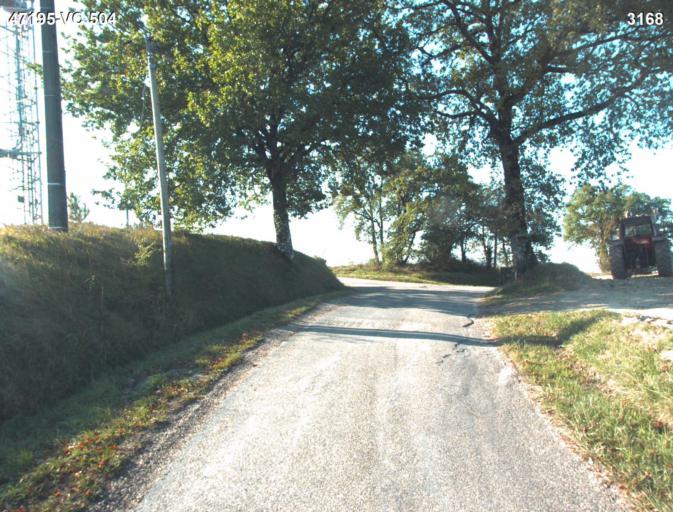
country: FR
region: Aquitaine
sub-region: Departement du Lot-et-Garonne
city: Vianne
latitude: 44.1726
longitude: 0.3433
